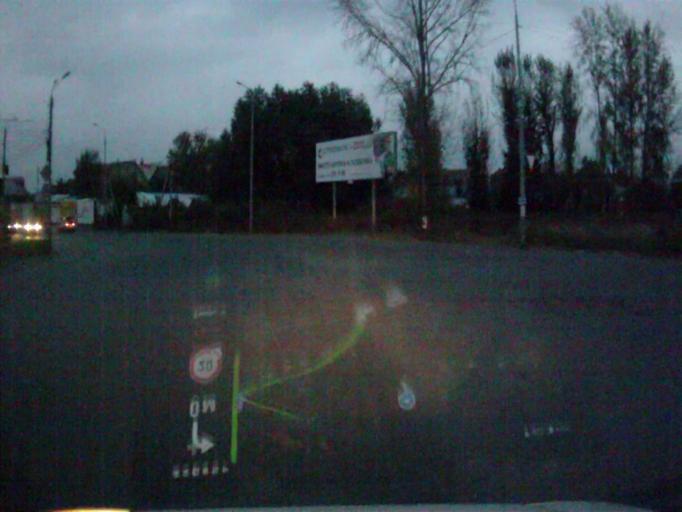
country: RU
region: Chelyabinsk
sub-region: Gorod Chelyabinsk
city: Chelyabinsk
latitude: 55.1567
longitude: 61.2988
